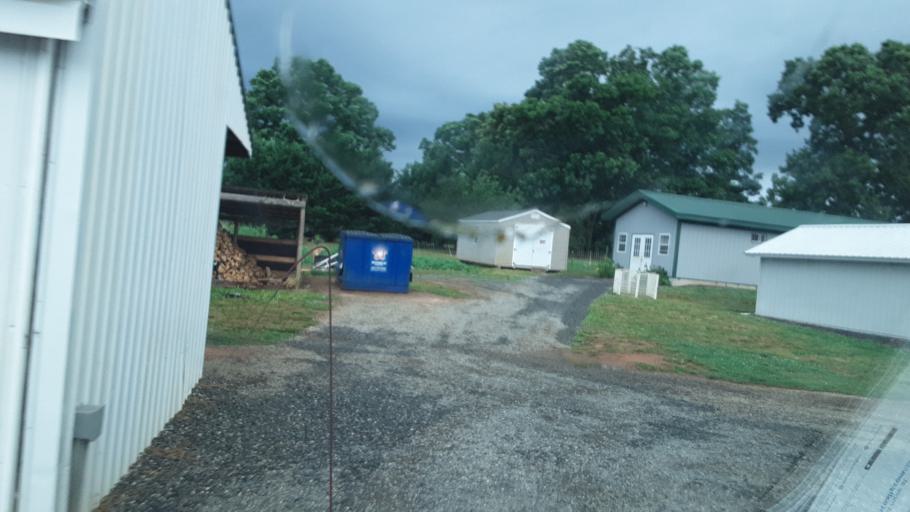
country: US
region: North Carolina
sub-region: Yadkin County
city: Jonesville
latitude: 36.0789
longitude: -80.8748
